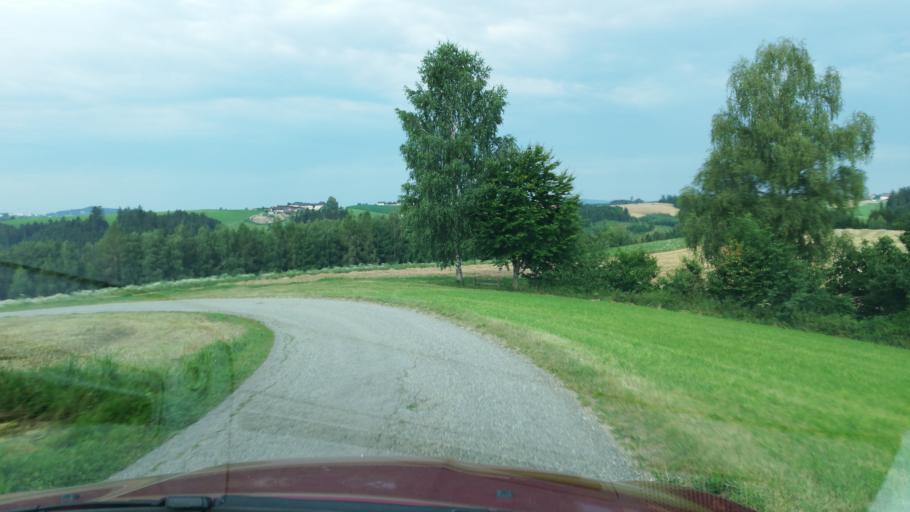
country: AT
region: Upper Austria
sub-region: Politischer Bezirk Rohrbach
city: Kleinzell im Muehlkreis
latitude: 48.5051
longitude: 14.0157
